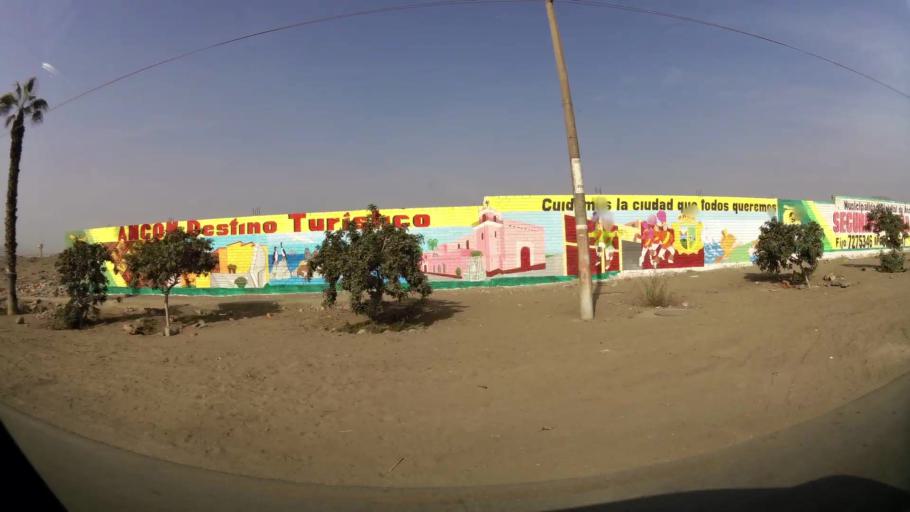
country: PE
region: Lima
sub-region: Lima
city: Santa Rosa
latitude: -11.7704
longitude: -77.1700
